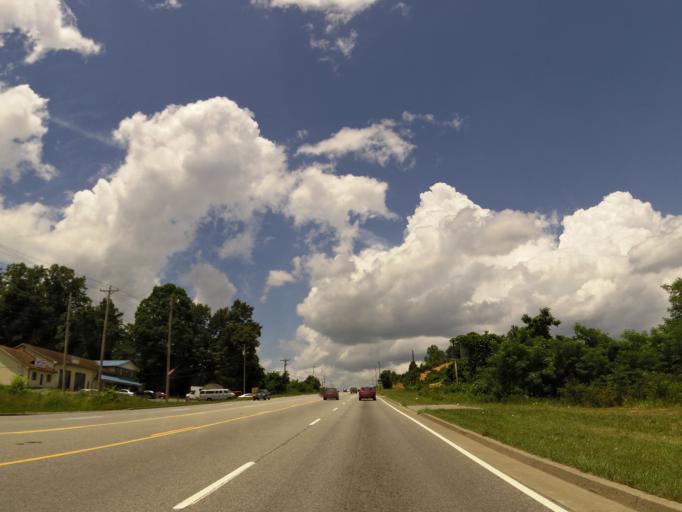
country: US
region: Tennessee
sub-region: Claiborne County
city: Tazewell
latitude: 36.4663
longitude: -83.5729
